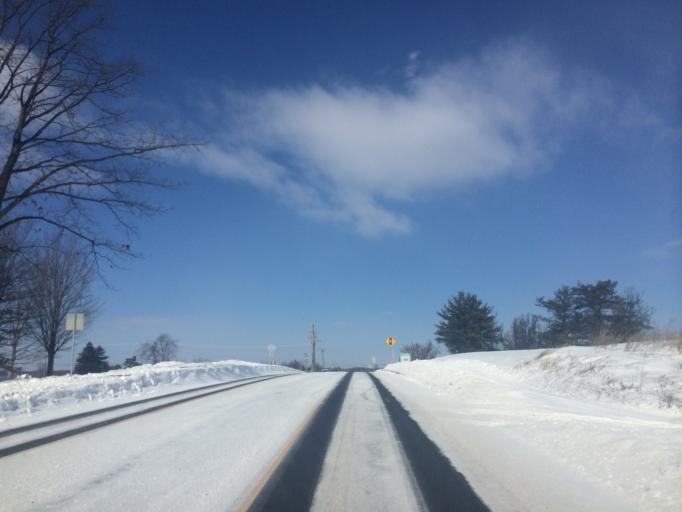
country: US
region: Pennsylvania
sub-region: Centre County
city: Park Forest Village
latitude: 40.7770
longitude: -77.8948
